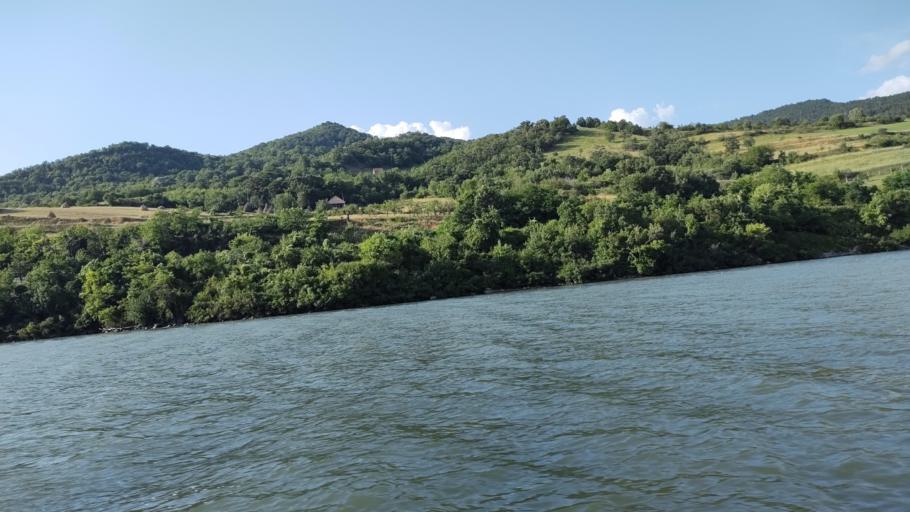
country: RO
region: Mehedinti
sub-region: Comuna Svinita
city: Svinita
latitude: 44.4797
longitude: 22.1303
